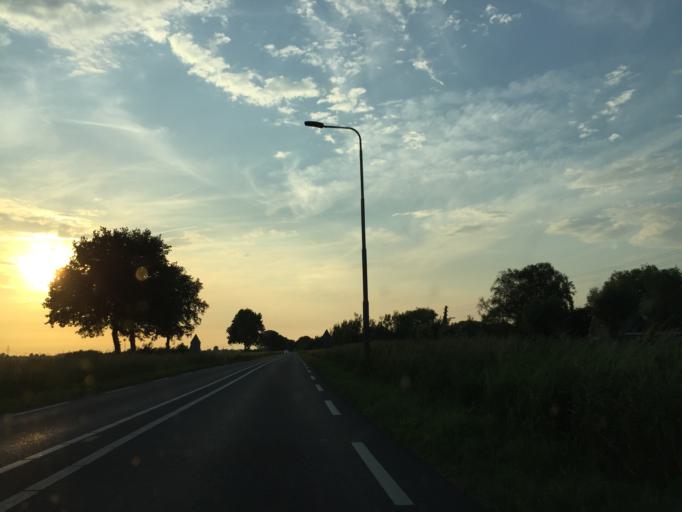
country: NL
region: South Holland
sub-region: Gemeente Vlist
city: Haastrecht
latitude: 51.9776
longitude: 4.7629
